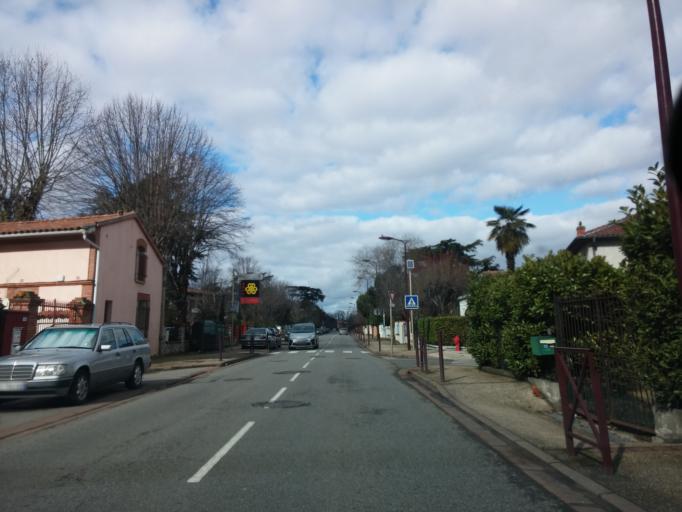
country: FR
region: Midi-Pyrenees
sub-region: Departement de la Haute-Garonne
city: Blagnac
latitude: 43.6267
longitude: 1.3984
